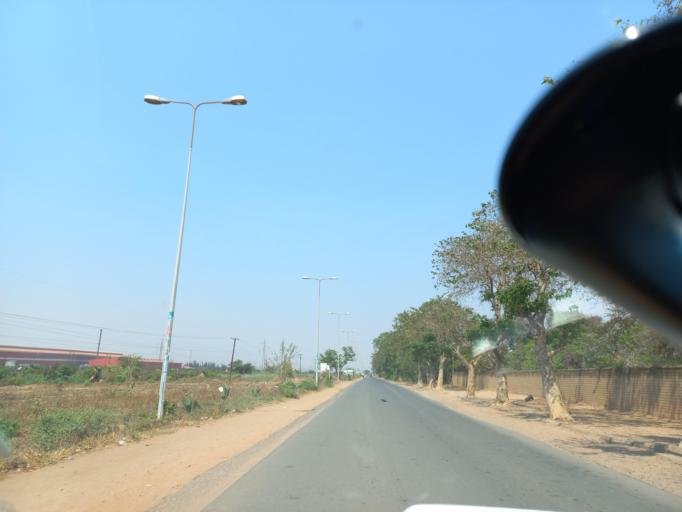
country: ZM
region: Lusaka
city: Kafue
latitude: -15.7448
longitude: 28.1685
